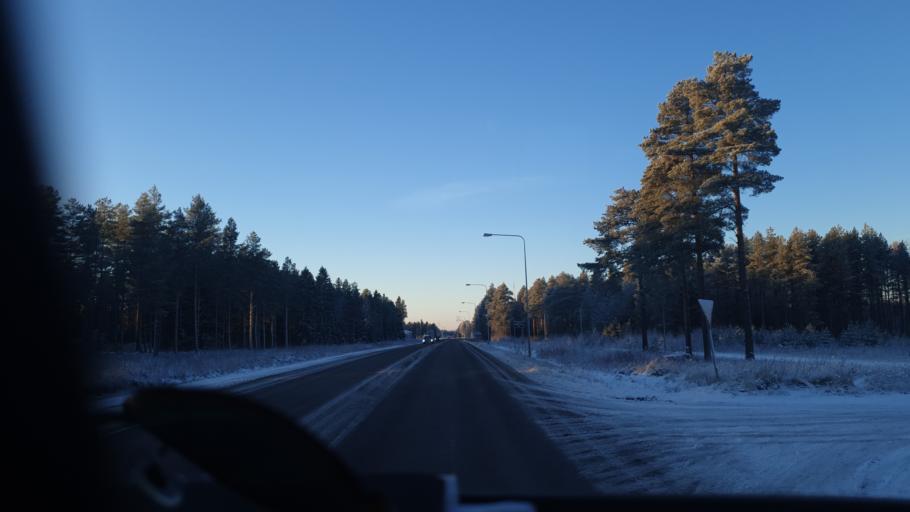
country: FI
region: Northern Ostrobothnia
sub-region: Ylivieska
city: Kalajoki
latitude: 64.2499
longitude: 23.9016
